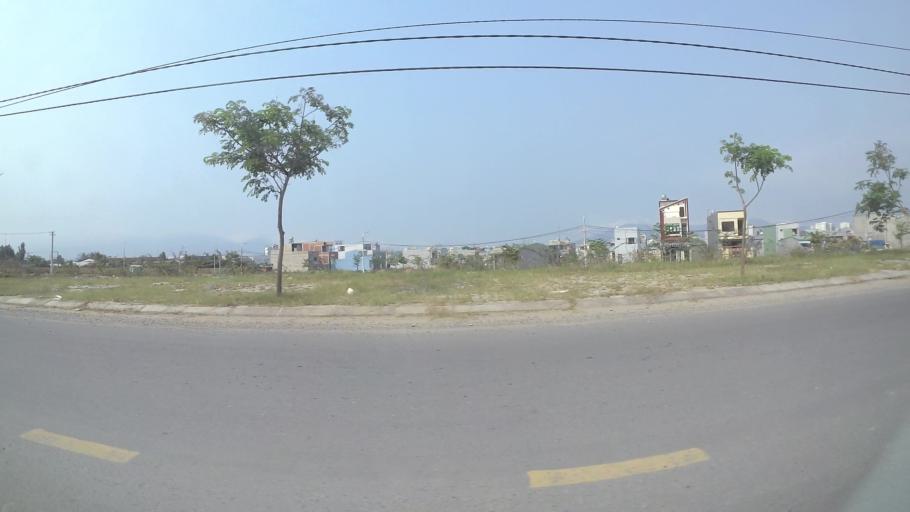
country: VN
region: Da Nang
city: Lien Chieu
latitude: 16.0415
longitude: 108.1668
